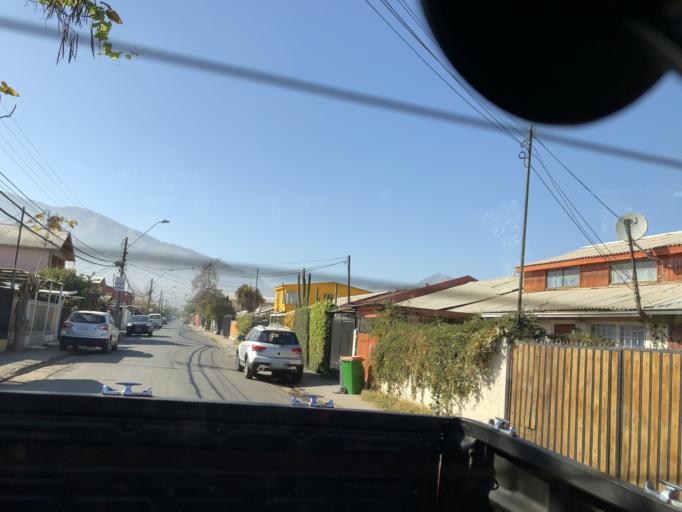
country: CL
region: Santiago Metropolitan
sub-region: Provincia de Cordillera
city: Puente Alto
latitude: -33.5734
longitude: -70.5756
